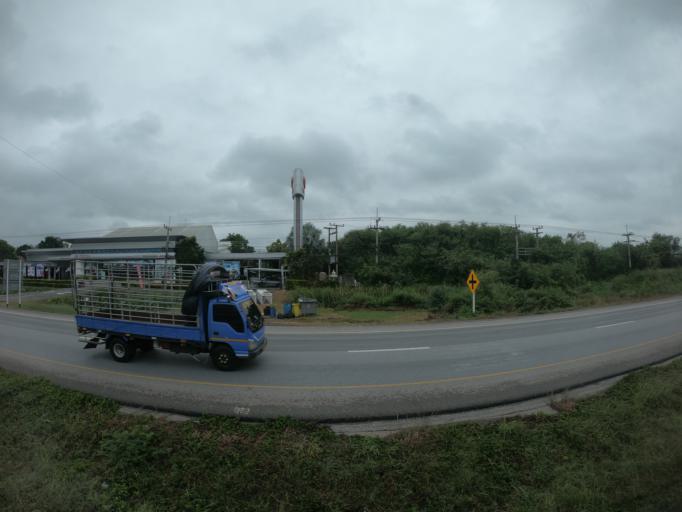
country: TH
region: Nakhon Ratchasima
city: Sida
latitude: 15.5430
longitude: 102.5470
